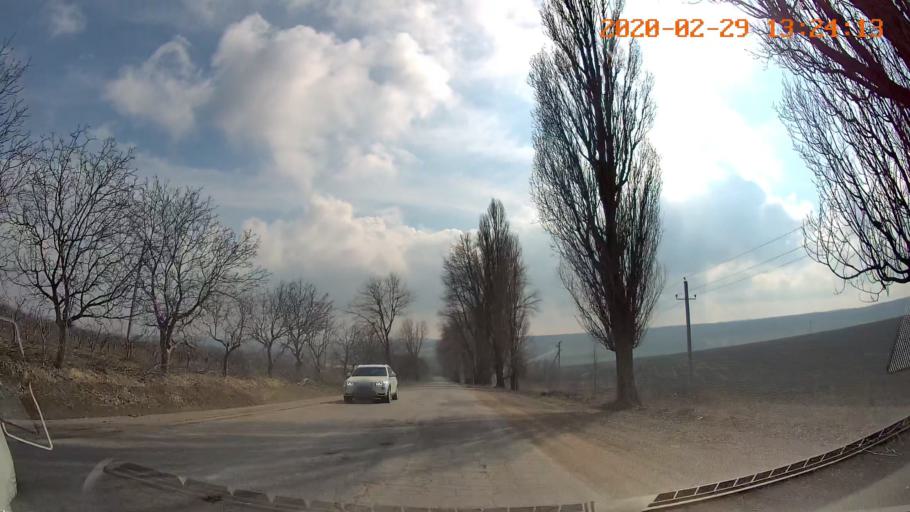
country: MD
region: Telenesti
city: Camenca
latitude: 47.9412
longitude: 28.6264
